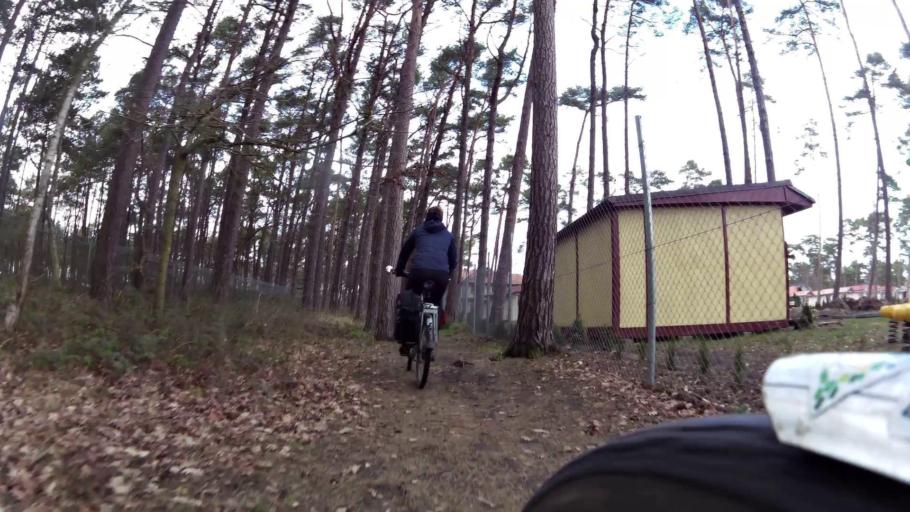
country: PL
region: West Pomeranian Voivodeship
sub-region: Powiat kamienski
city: Dziwnow
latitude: 54.0353
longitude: 14.8004
